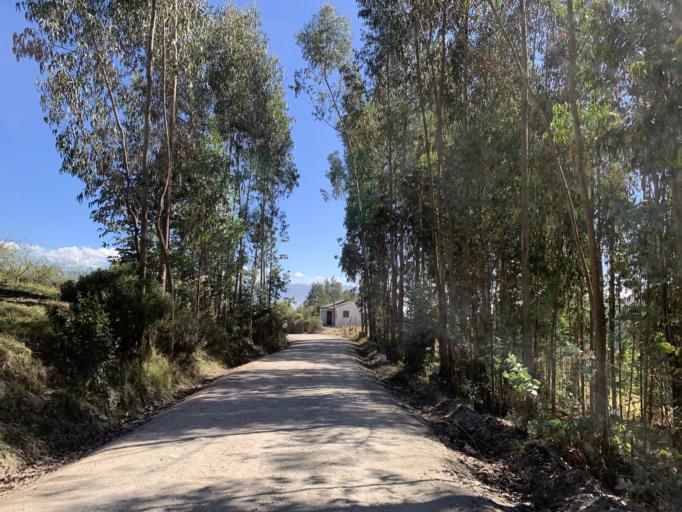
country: CO
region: Boyaca
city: Tuta
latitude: 5.7111
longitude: -73.1537
